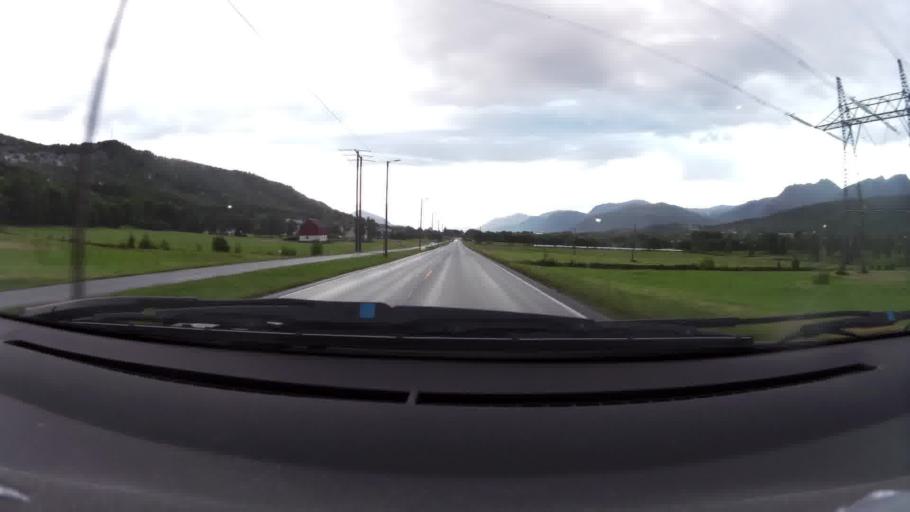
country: NO
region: More og Romsdal
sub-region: Eide
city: Eide
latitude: 62.8885
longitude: 7.3583
